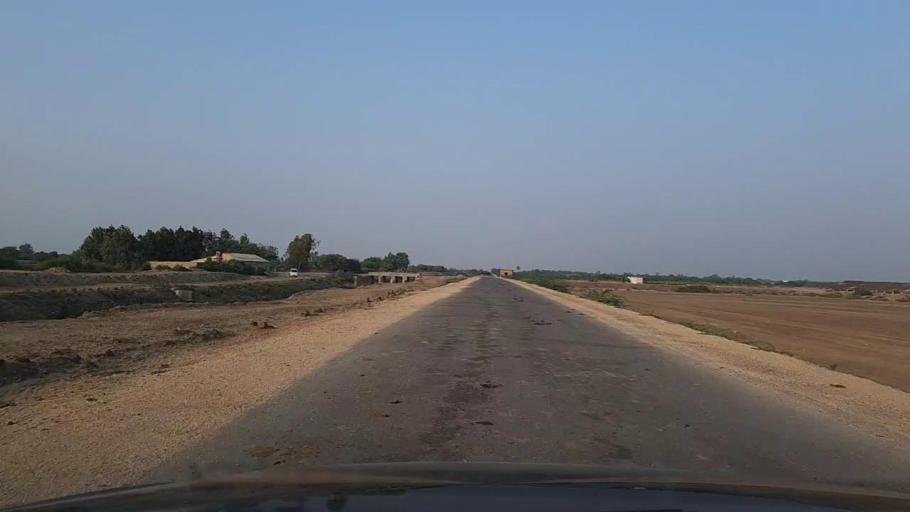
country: PK
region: Sindh
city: Mirpur Sakro
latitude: 24.4855
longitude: 67.8071
